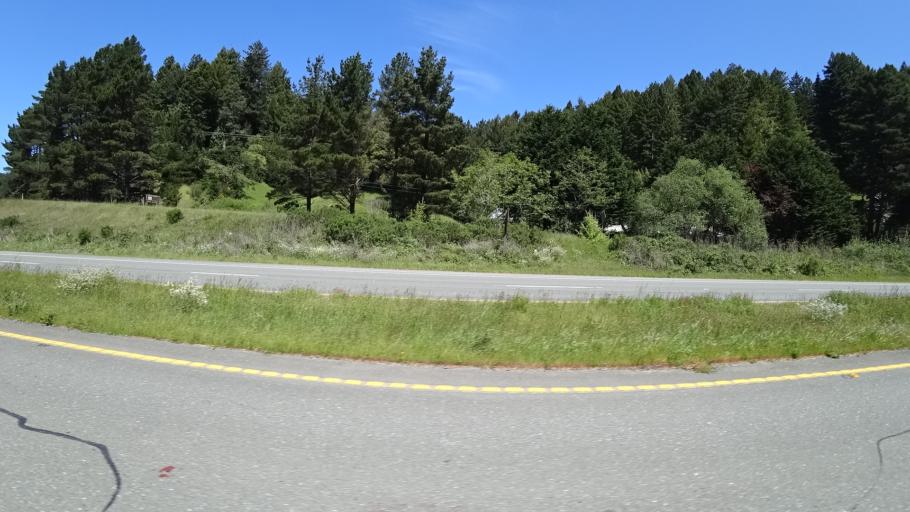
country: US
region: California
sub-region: Humboldt County
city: Arcata
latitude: 40.9099
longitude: -124.0574
